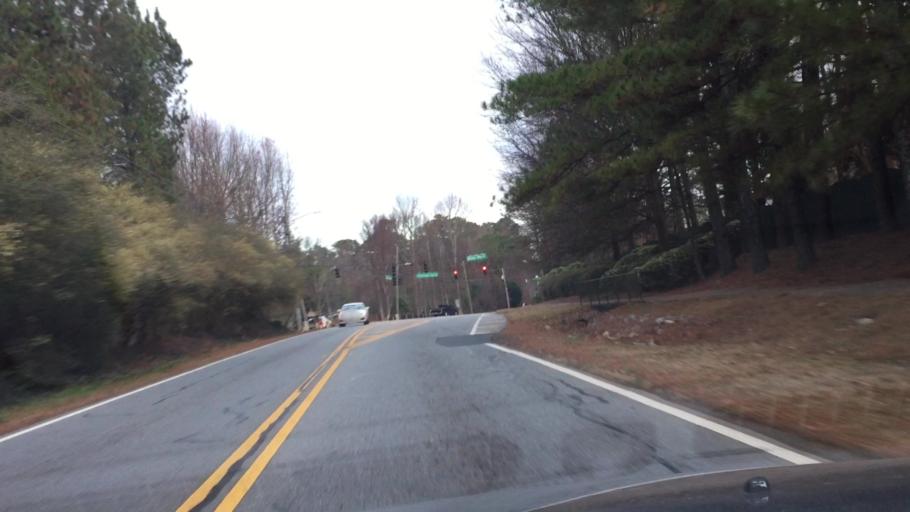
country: US
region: Georgia
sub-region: DeKalb County
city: Doraville
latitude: 33.9536
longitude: -84.2722
